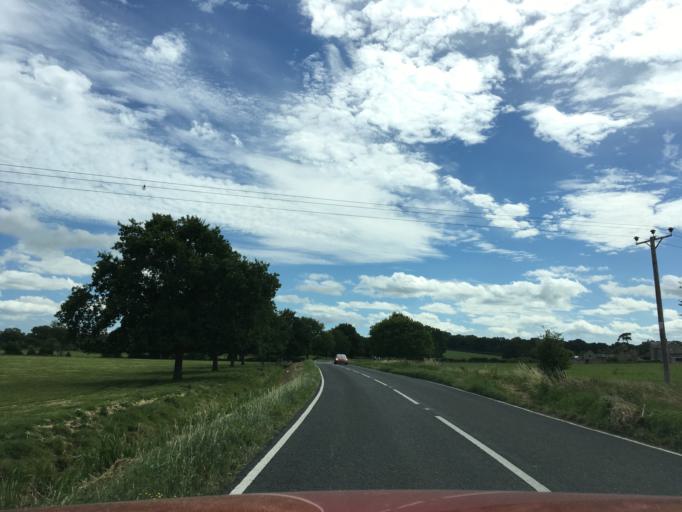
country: GB
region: England
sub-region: Somerset
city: Glastonbury
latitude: 51.1238
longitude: -2.7113
